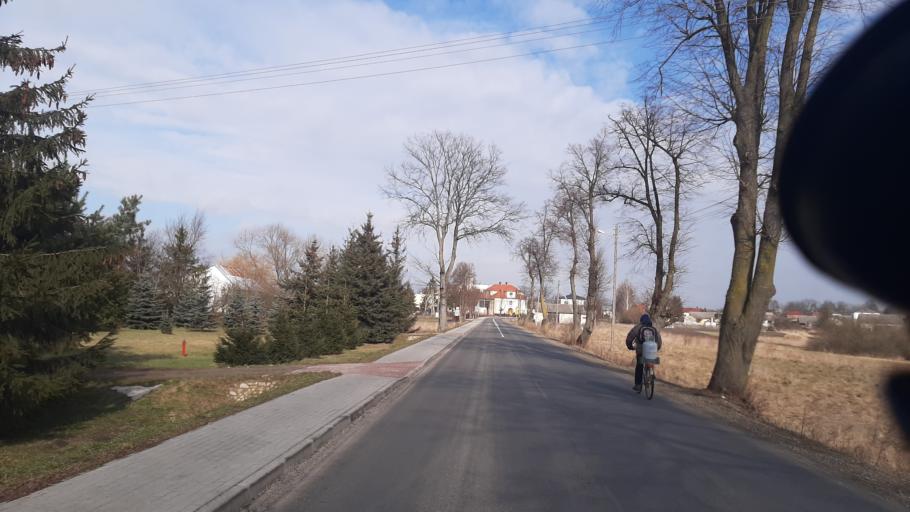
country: PL
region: Lublin Voivodeship
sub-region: Powiat lubartowski
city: Wola Sernicka
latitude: 51.4506
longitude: 22.6704
